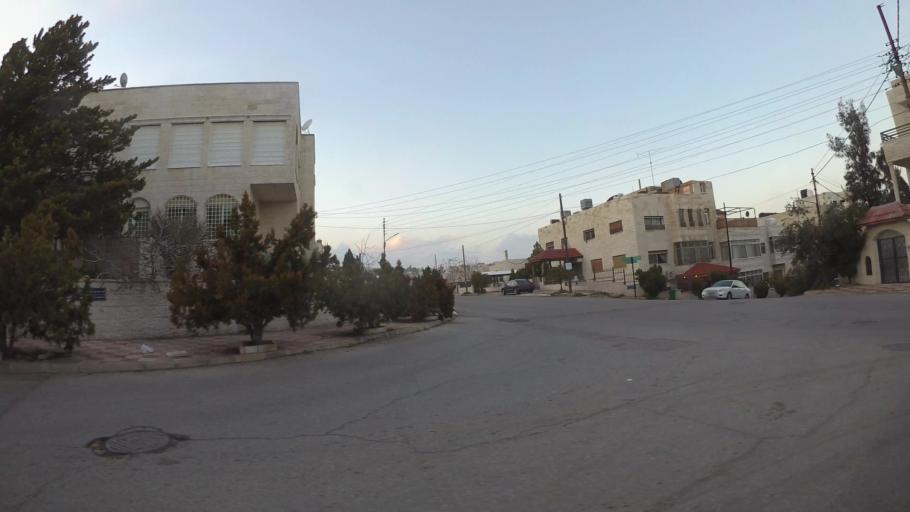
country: JO
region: Amman
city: Amman
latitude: 31.9977
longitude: 35.9509
